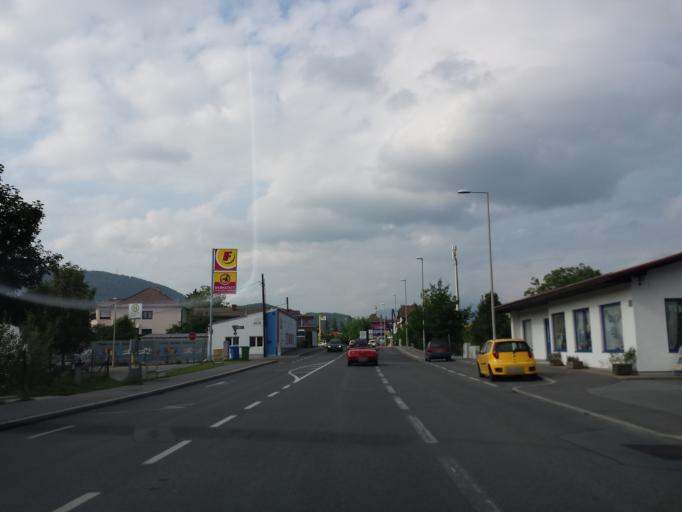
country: AT
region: Styria
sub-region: Graz Stadt
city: Wetzelsdorf
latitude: 47.0575
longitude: 15.3955
